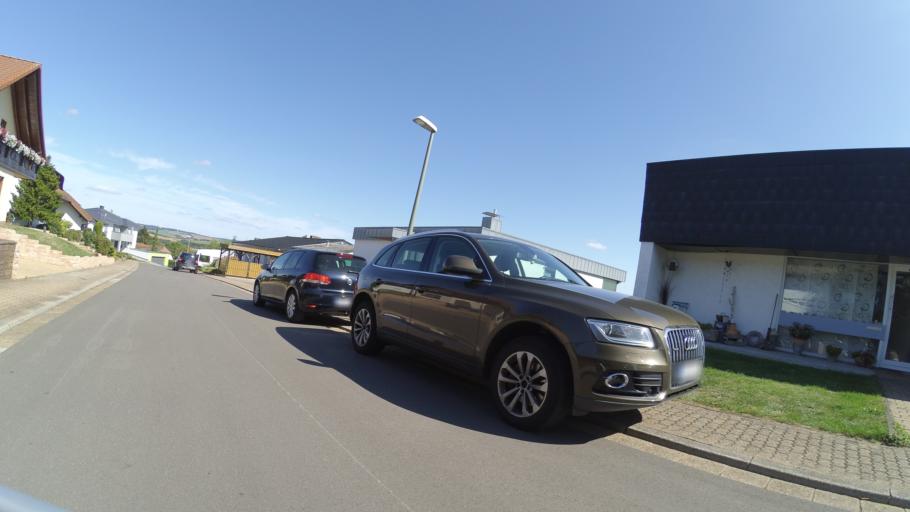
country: DE
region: Saarland
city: Lebach
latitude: 49.3883
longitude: 6.9020
